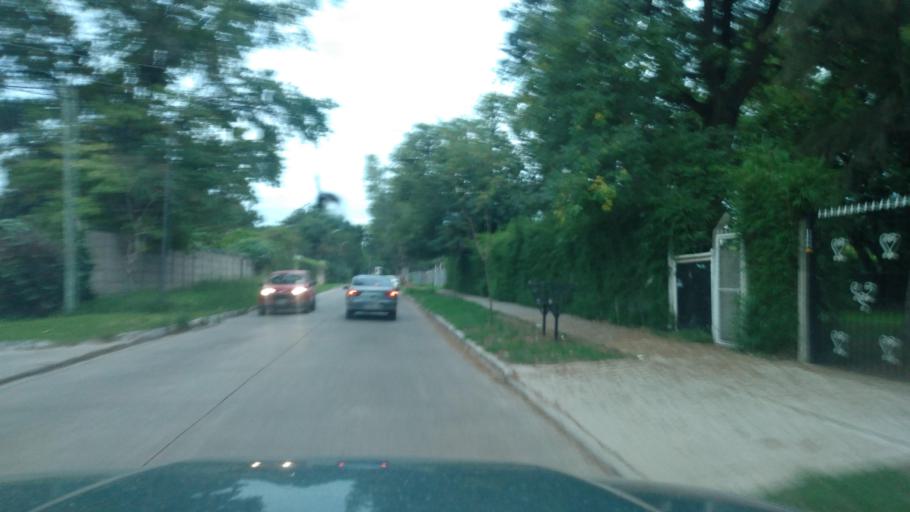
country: AR
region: Buenos Aires
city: Hurlingham
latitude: -34.5589
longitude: -58.7257
